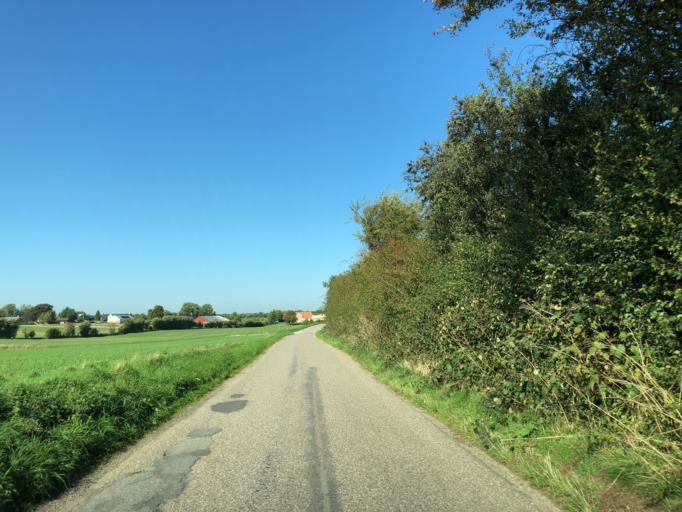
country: DK
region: South Denmark
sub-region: Sonderborg Kommune
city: Dybbol
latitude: 54.9500
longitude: 9.7293
